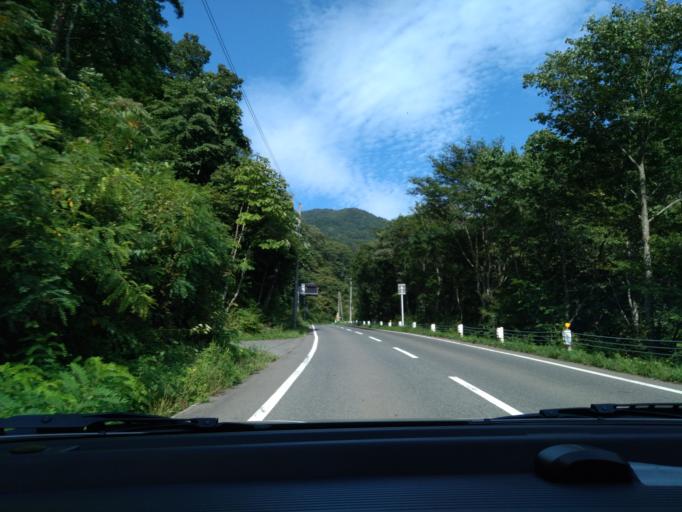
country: JP
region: Iwate
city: Shizukuishi
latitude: 39.6382
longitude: 141.0313
